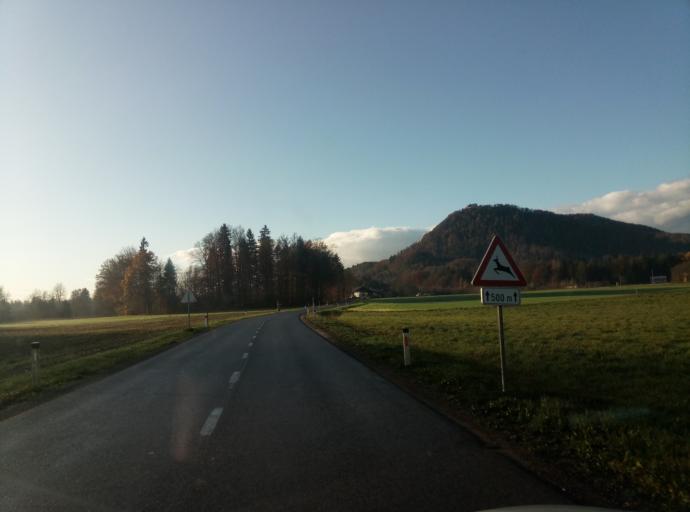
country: SI
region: Vodice
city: Vodice
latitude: 46.1458
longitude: 14.4803
